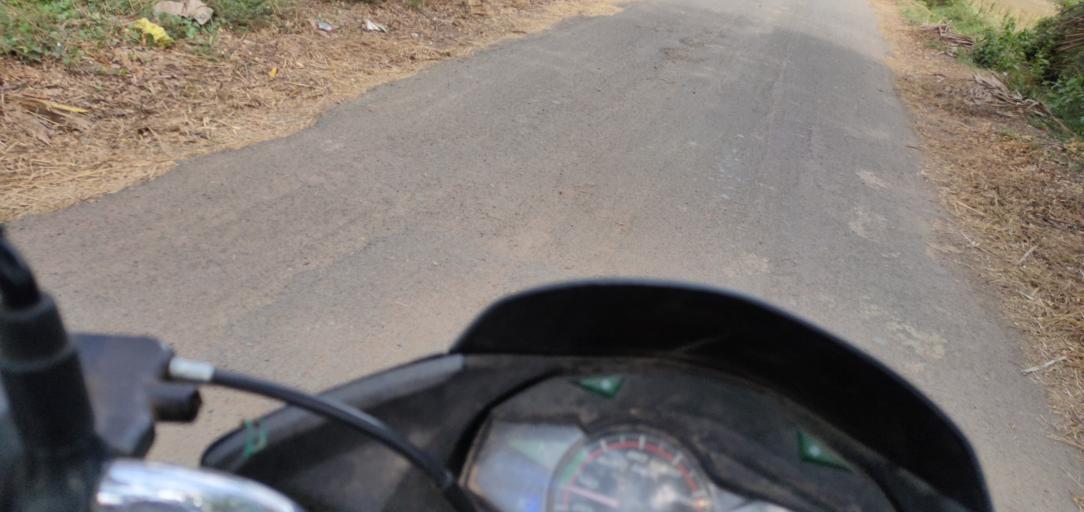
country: IN
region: Andhra Pradesh
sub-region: West Godavari
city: Tadepallegudem
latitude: 16.8505
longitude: 81.4947
